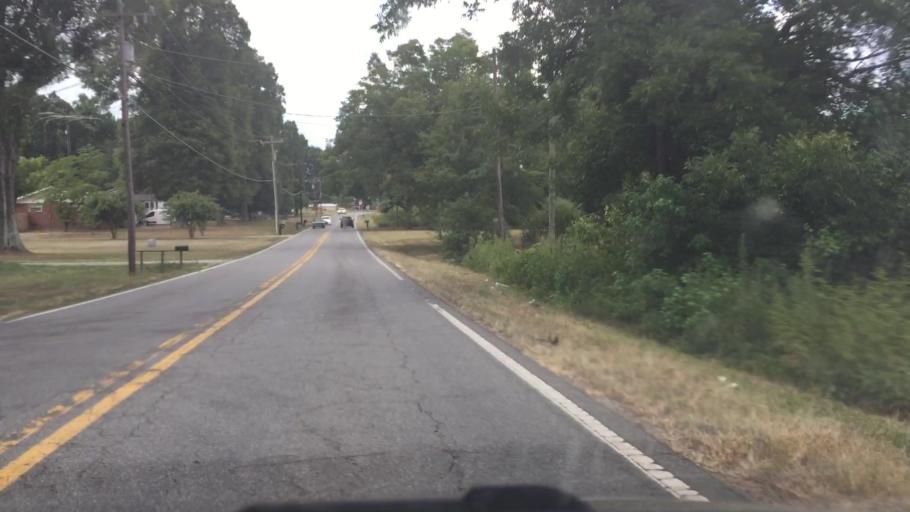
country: US
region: North Carolina
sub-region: Rowan County
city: Enochville
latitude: 35.5210
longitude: -80.6699
